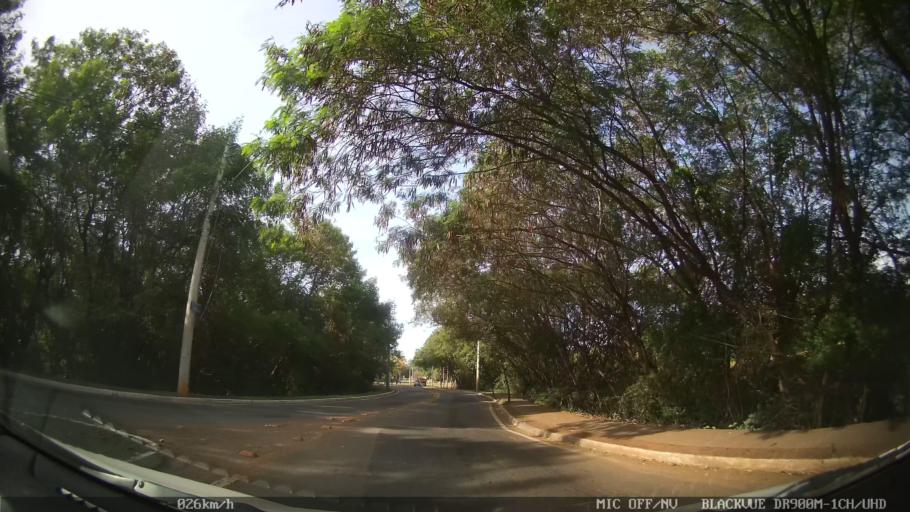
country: BR
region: Sao Paulo
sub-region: Piracicaba
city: Piracicaba
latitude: -22.7322
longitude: -47.6725
